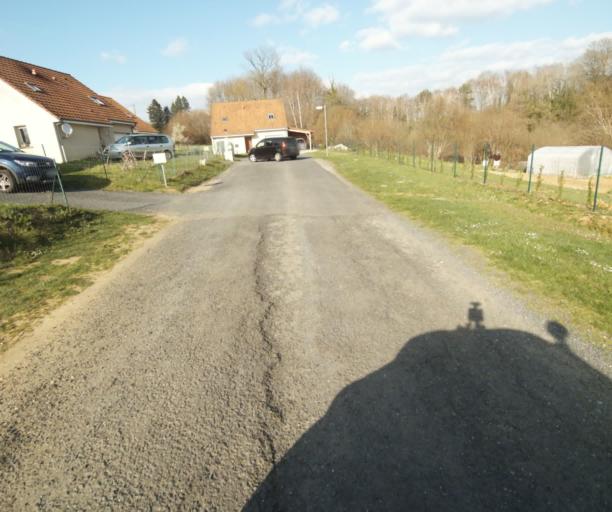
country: FR
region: Limousin
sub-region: Departement de la Correze
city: Saint-Clement
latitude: 45.3483
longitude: 1.6270
